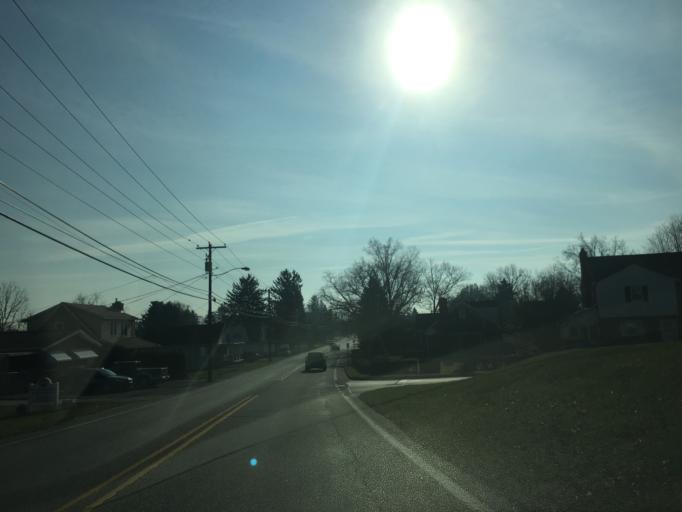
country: US
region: Pennsylvania
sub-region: Dauphin County
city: Progress
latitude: 40.2830
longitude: -76.8397
